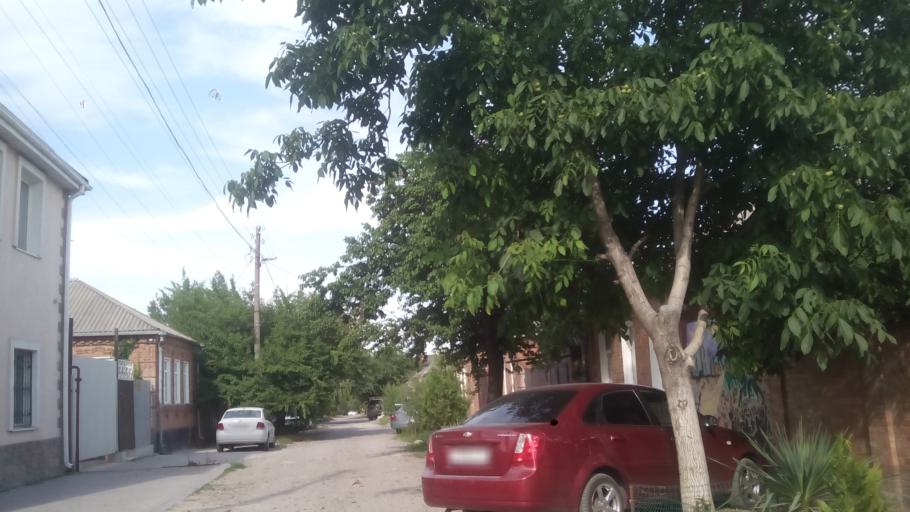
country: RU
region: Rostov
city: Rostov-na-Donu
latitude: 47.2265
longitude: 39.6380
